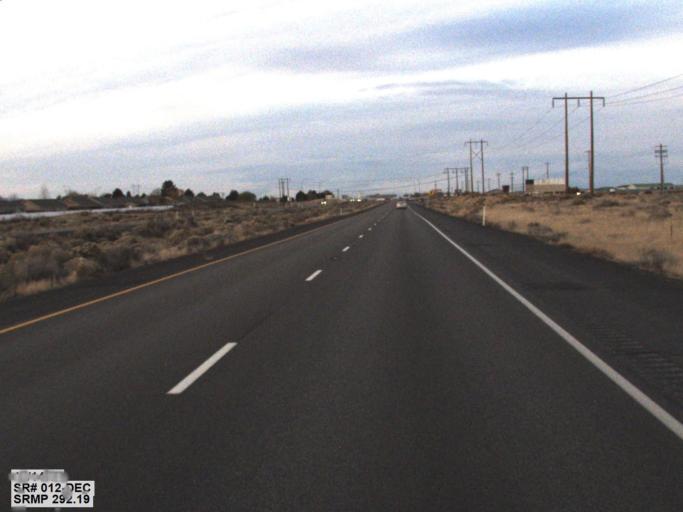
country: US
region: Washington
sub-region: Franklin County
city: Pasco
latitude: 46.2416
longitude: -119.0597
